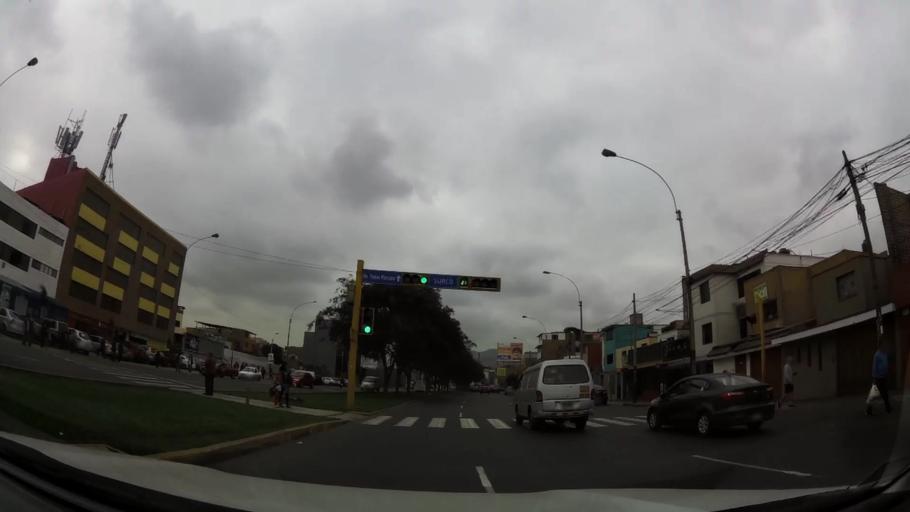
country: PE
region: Lima
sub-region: Lima
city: Surco
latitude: -12.1510
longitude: -76.9884
